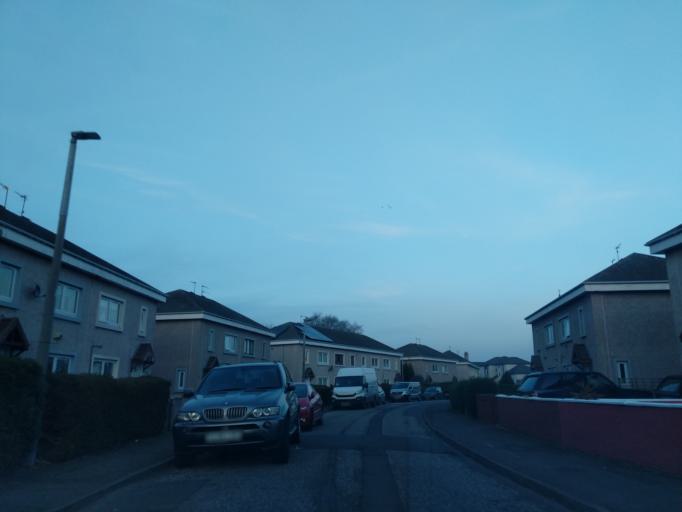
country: GB
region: Scotland
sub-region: Edinburgh
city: Colinton
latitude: 55.9312
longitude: -3.2682
